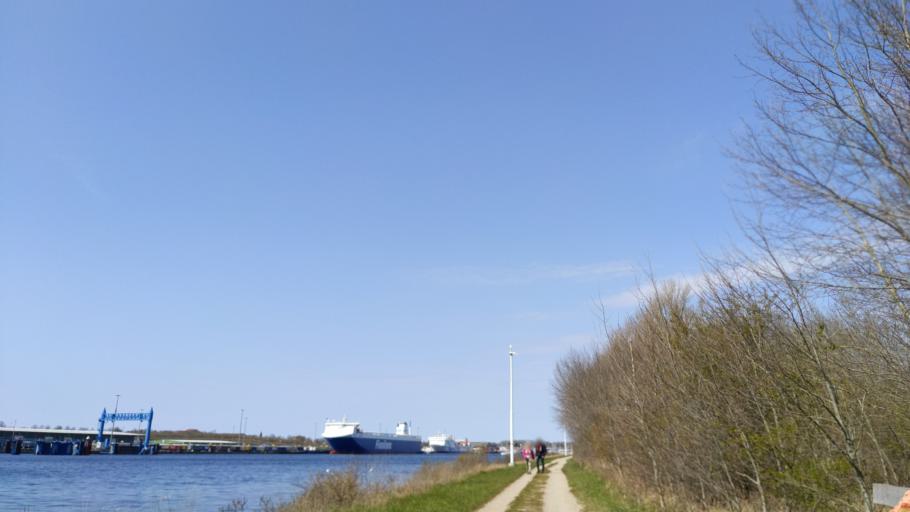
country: DE
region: Schleswig-Holstein
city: Travemuende
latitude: 53.9417
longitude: 10.8658
